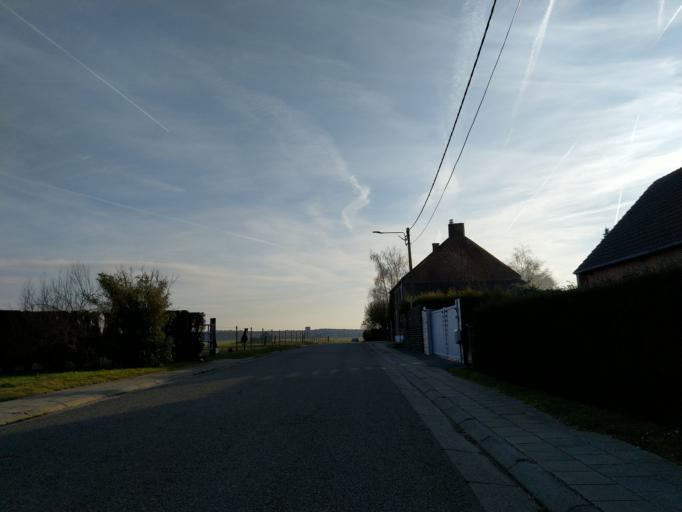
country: BE
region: Wallonia
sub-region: Province du Hainaut
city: Jurbise
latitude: 50.5234
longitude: 3.9100
